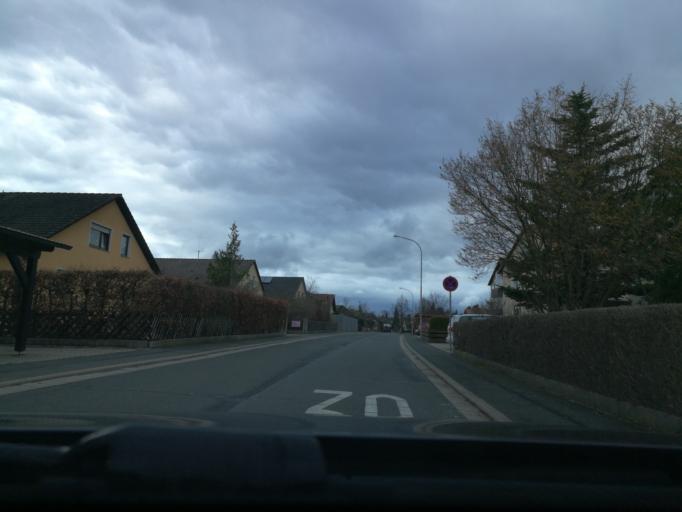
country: DE
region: Bavaria
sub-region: Regierungsbezirk Mittelfranken
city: Hemhofen
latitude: 49.6880
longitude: 10.9386
